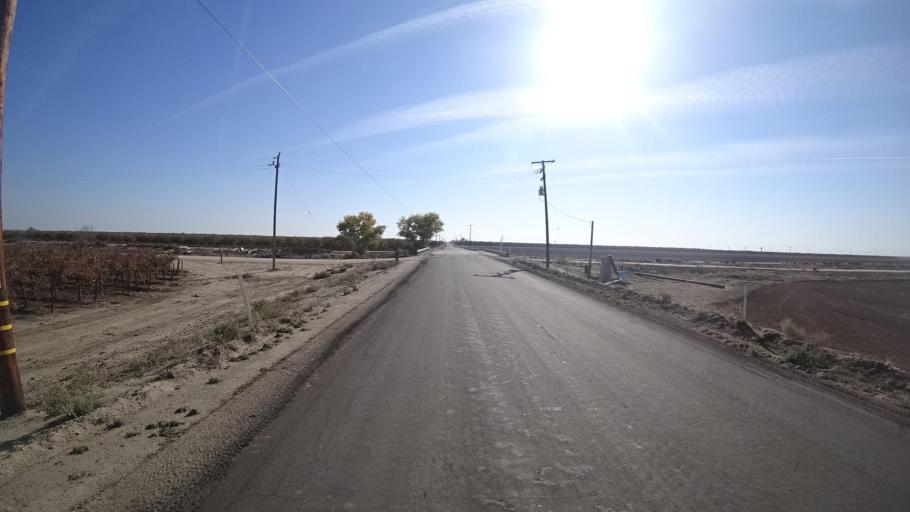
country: US
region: California
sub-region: Kern County
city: Wasco
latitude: 35.6817
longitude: -119.3840
